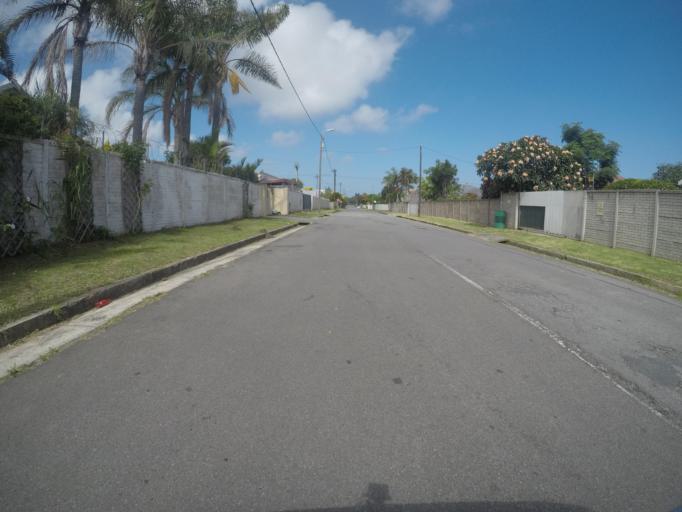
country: ZA
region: Eastern Cape
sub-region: Buffalo City Metropolitan Municipality
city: East London
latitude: -32.9827
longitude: 27.9072
